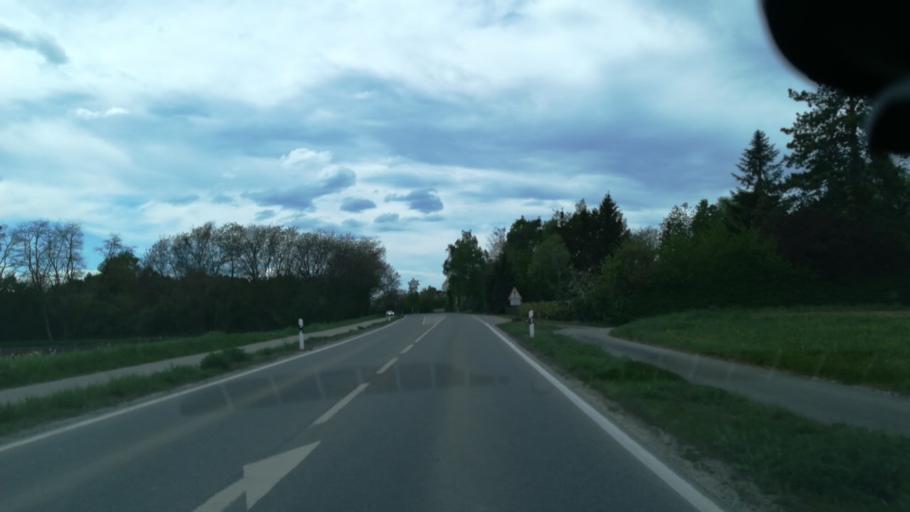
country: DE
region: Baden-Wuerttemberg
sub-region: Freiburg Region
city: Radolfzell am Bodensee
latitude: 47.7471
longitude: 8.9928
